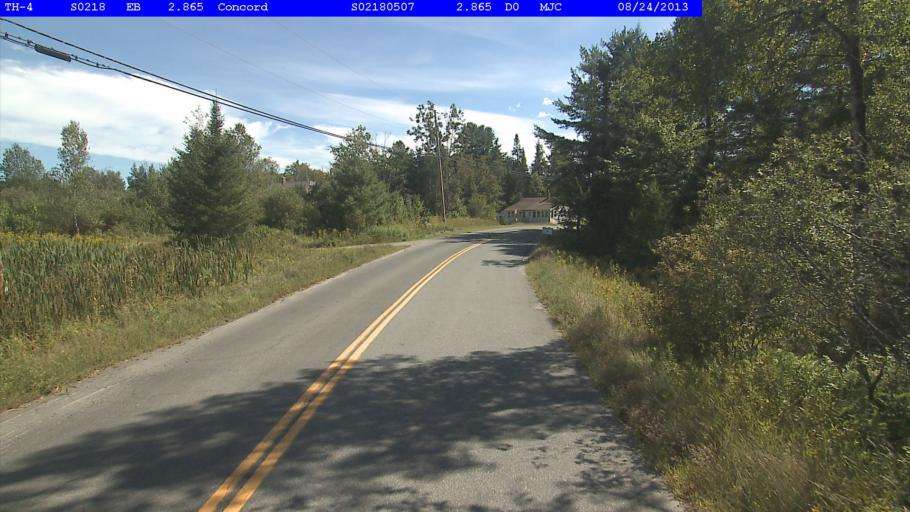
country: US
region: New Hampshire
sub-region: Grafton County
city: Littleton
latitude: 44.4277
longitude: -71.7518
